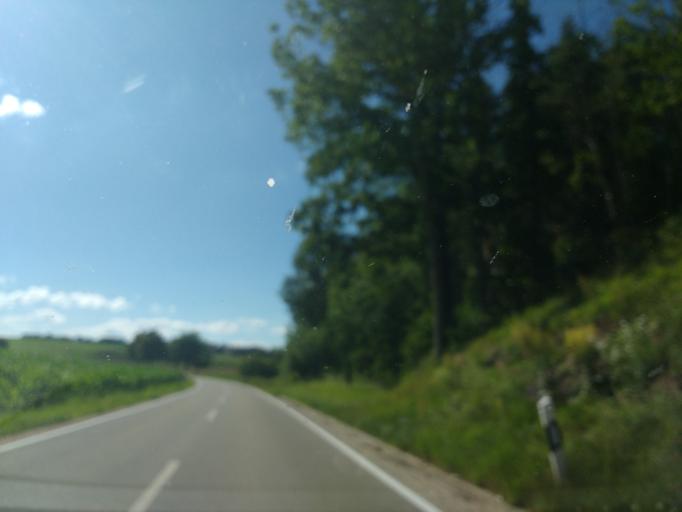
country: DE
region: Bavaria
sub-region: Upper Bavaria
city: Engelsberg
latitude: 48.1217
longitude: 12.5297
